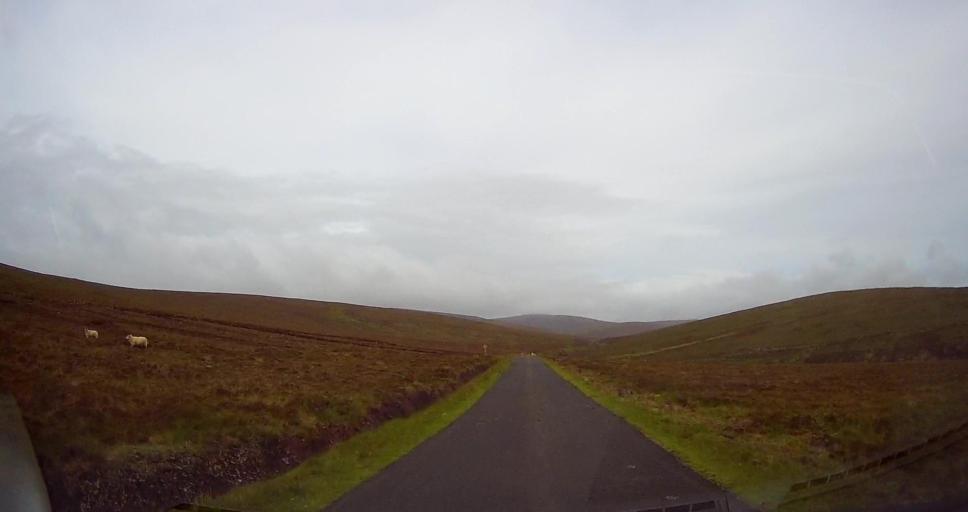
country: GB
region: Scotland
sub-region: Orkney Islands
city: Stromness
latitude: 58.8584
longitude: -3.2187
